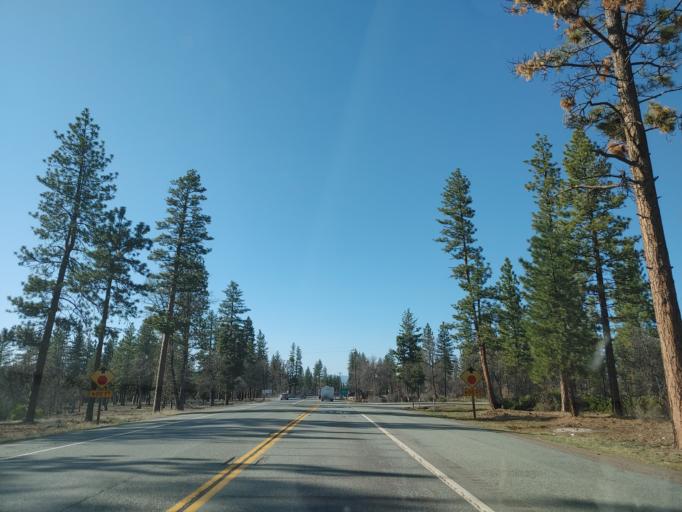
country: US
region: California
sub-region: Shasta County
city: Burney
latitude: 40.9361
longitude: -121.6054
